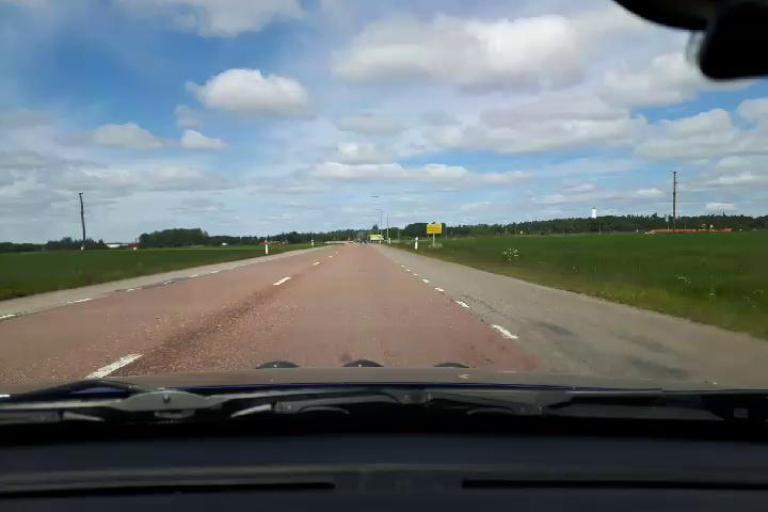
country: SE
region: Uppsala
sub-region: Osthammars Kommun
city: Bjorklinge
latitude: 60.0147
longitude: 17.5581
